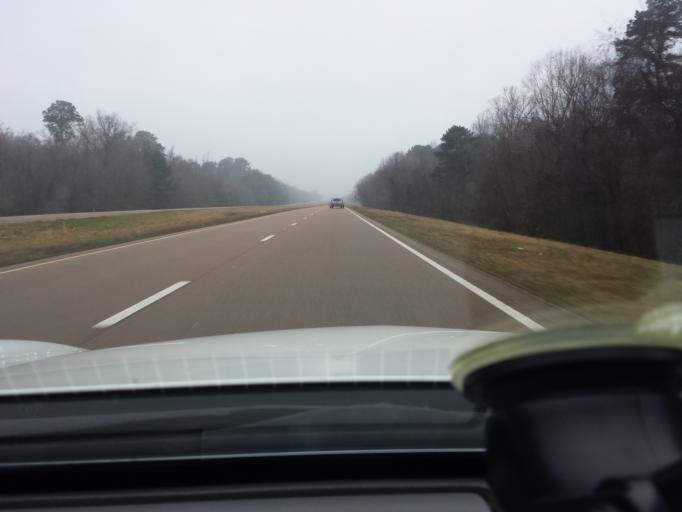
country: US
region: Mississippi
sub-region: Leake County
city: Carthage
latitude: 32.6789
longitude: -89.6400
